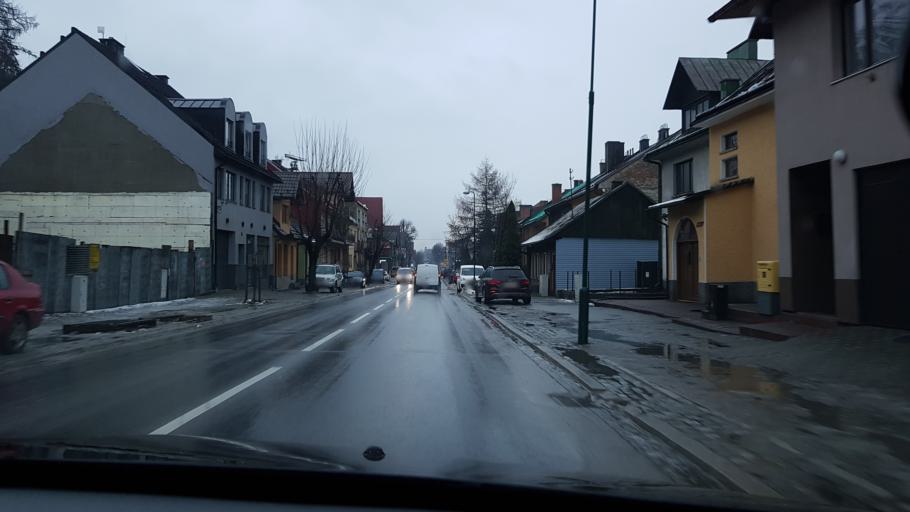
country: PL
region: Lesser Poland Voivodeship
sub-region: Powiat nowotarski
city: Nowy Targ
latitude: 49.4868
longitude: 20.0245
